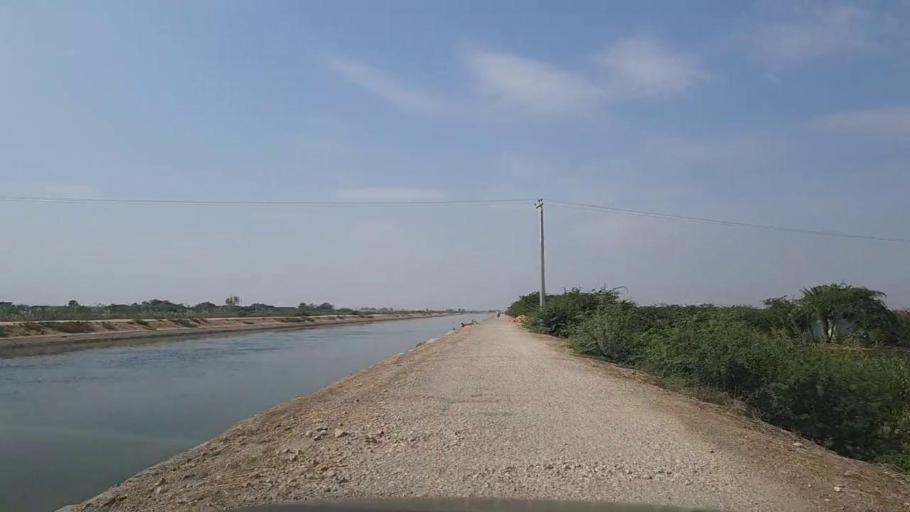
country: PK
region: Sindh
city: Thatta
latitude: 24.7536
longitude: 67.7665
